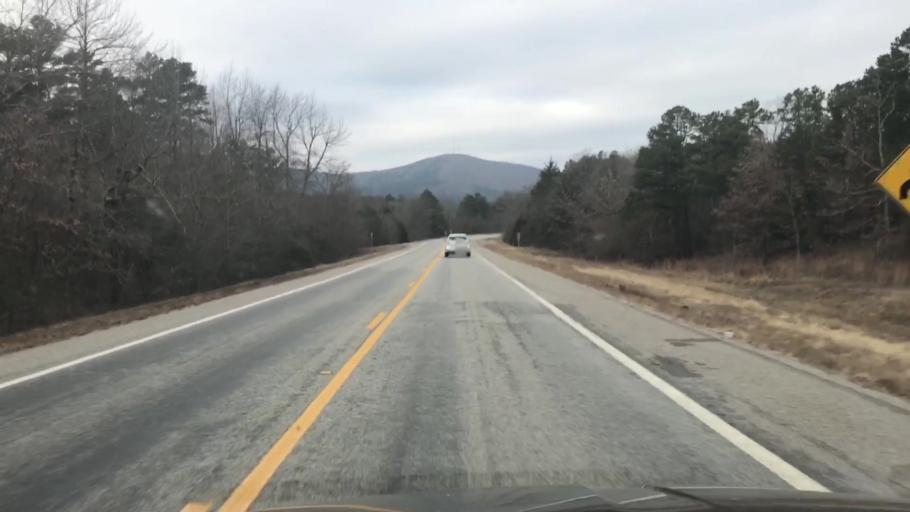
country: US
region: Arkansas
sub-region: Montgomery County
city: Mount Ida
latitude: 34.6878
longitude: -93.8881
